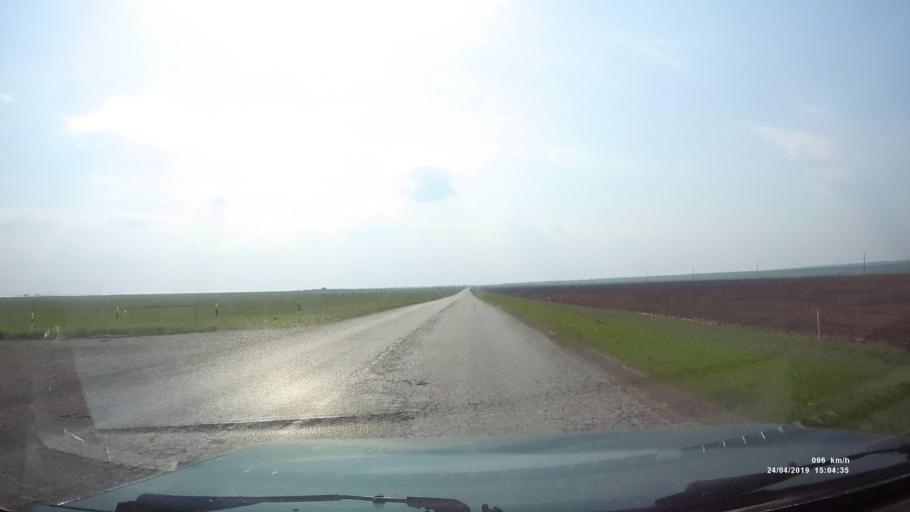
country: RU
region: Rostov
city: Remontnoye
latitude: 46.5618
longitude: 43.4673
